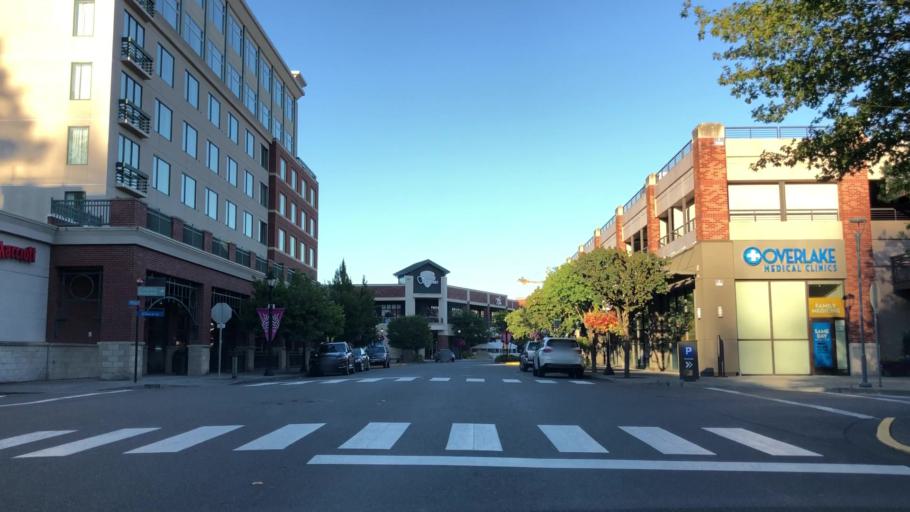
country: US
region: Washington
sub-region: King County
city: Redmond
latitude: 47.6707
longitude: -122.1232
